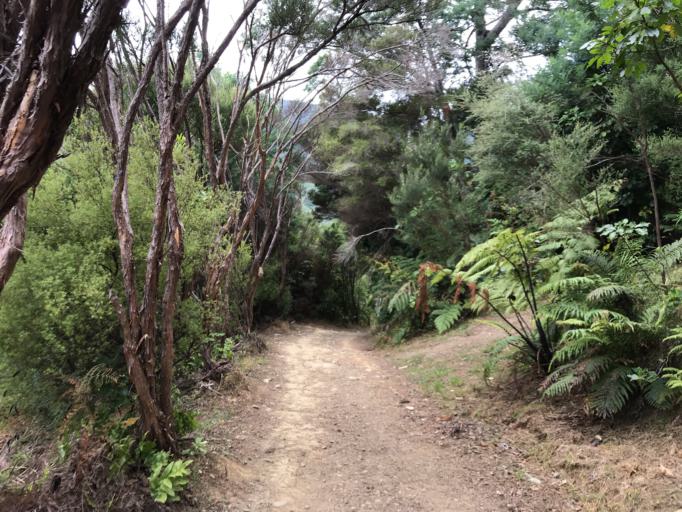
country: NZ
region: Marlborough
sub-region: Marlborough District
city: Picton
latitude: -41.1000
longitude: 174.1849
